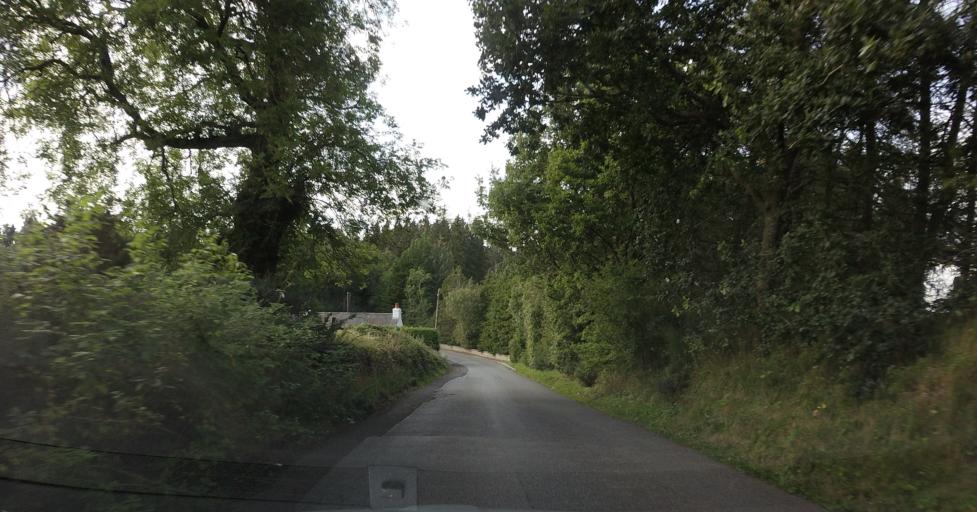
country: GB
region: Scotland
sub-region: Perth and Kinross
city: Auchterarder
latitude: 56.3060
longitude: -3.7278
